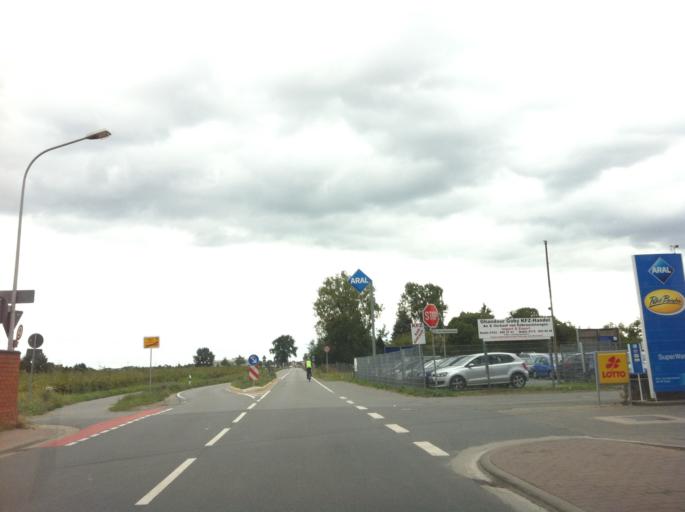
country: DE
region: Hesse
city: Pfungstadt
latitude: 49.8073
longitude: 8.5642
